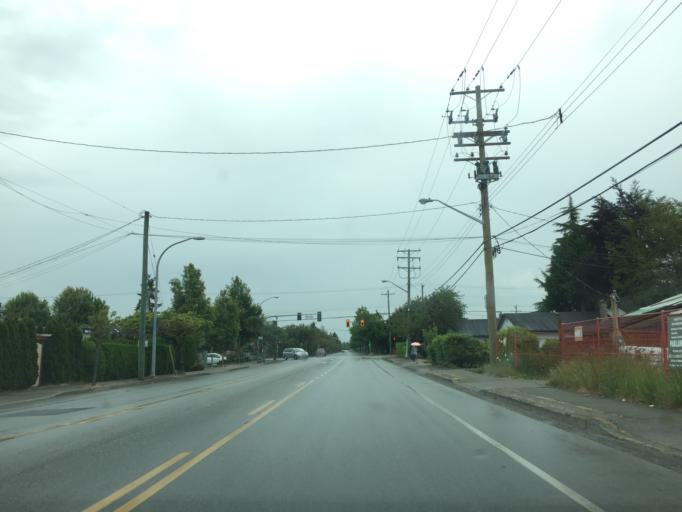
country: CA
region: British Columbia
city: Richmond
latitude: 49.1408
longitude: -123.1156
